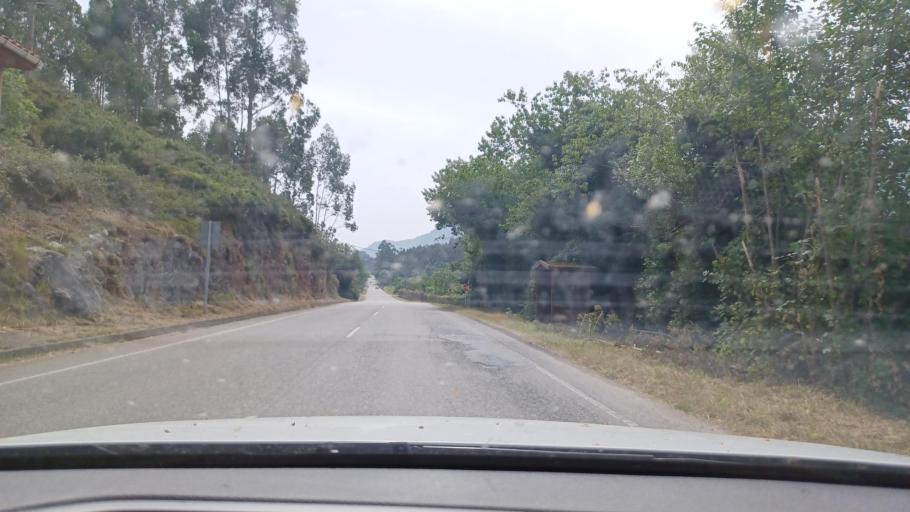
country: ES
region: Asturias
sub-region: Province of Asturias
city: Ribadesella
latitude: 43.4472
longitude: -5.0162
